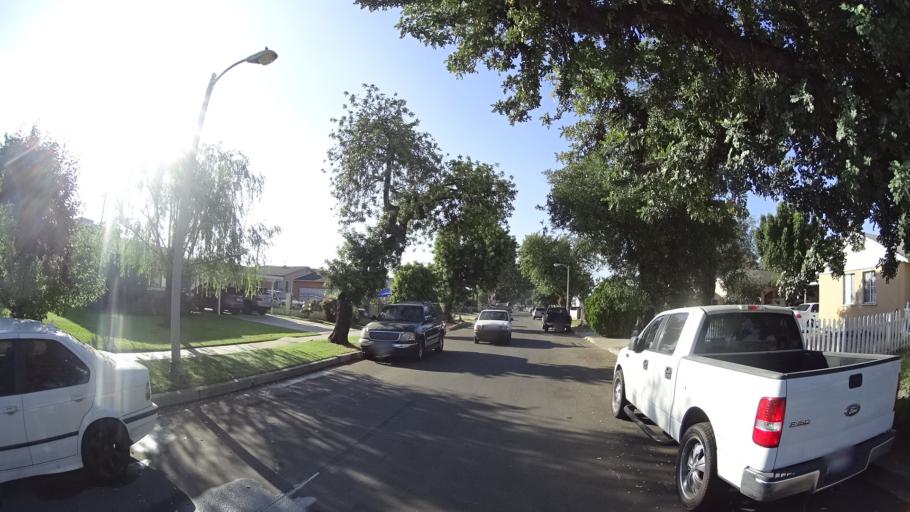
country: US
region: California
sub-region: Los Angeles County
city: San Fernando
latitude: 34.2335
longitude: -118.4205
